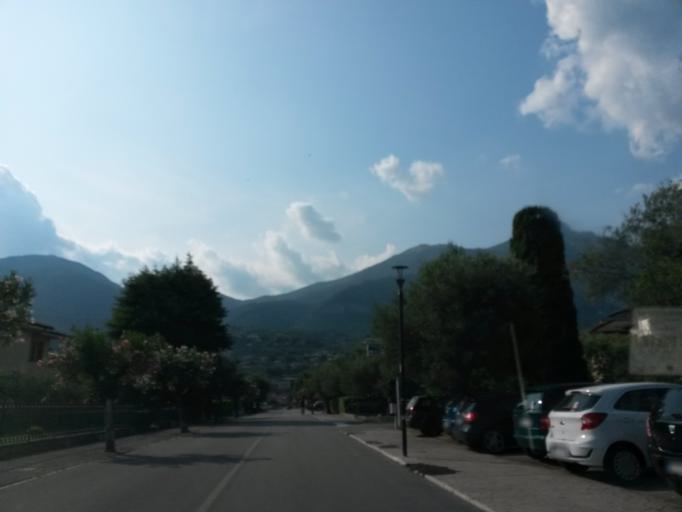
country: IT
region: Lombardy
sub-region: Provincia di Brescia
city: Toscolano Maderno
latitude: 45.6332
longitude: 10.6105
